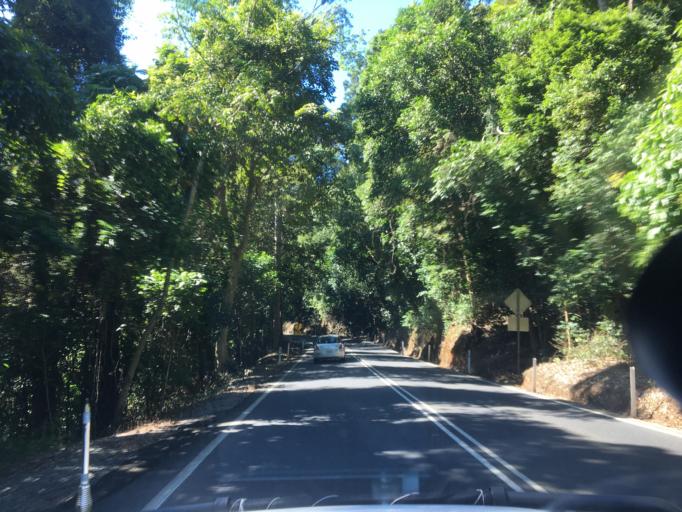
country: AU
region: Queensland
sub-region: Cairns
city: Redlynch
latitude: -16.8444
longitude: 145.6801
